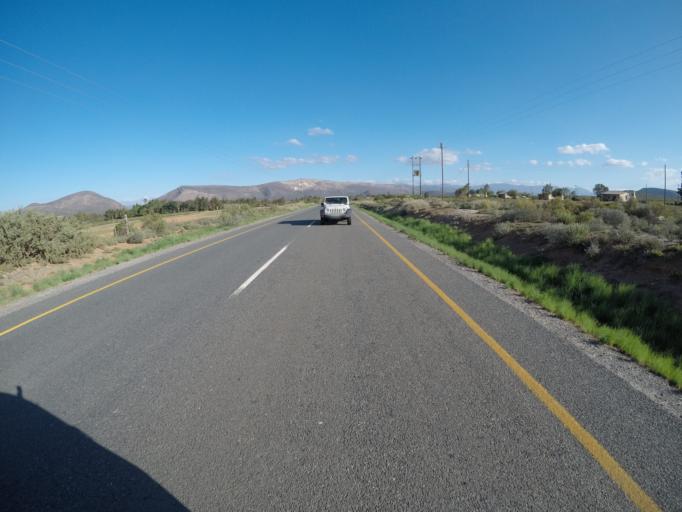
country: ZA
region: Western Cape
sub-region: Cape Winelands District Municipality
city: Ashton
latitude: -33.7996
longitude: 19.7813
